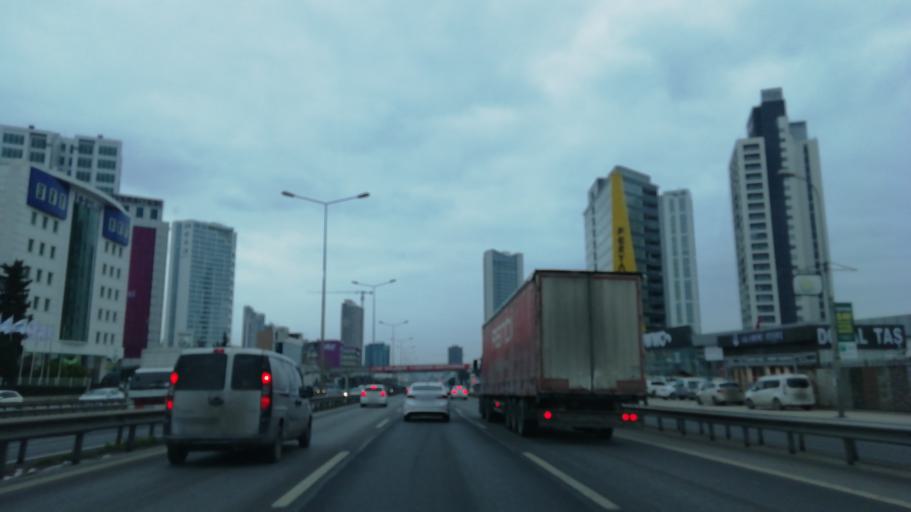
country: TR
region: Istanbul
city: Pendik
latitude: 40.9018
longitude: 29.2177
